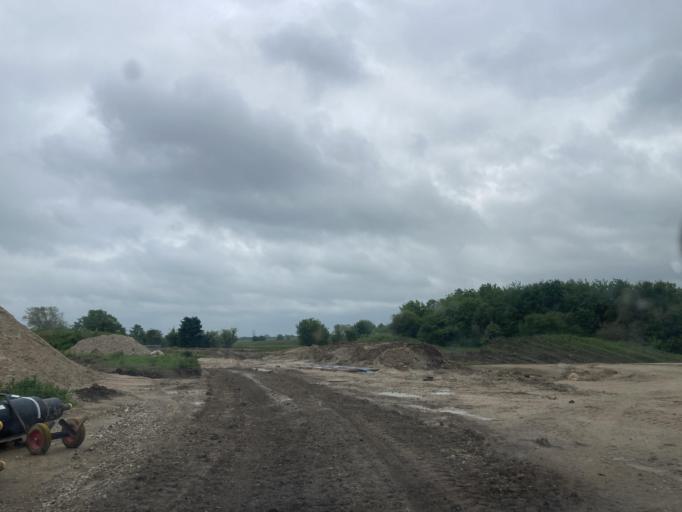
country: DK
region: Capital Region
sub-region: Hoje-Taastrup Kommune
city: Flong
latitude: 55.6409
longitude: 12.2092
